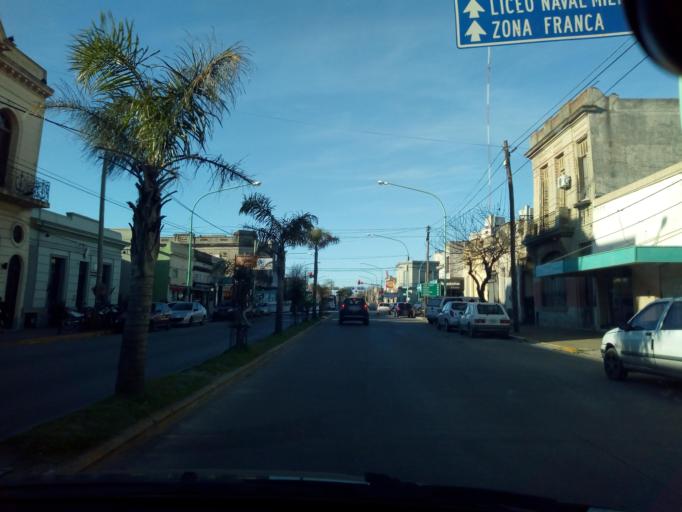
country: AR
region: Buenos Aires
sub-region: Partido de Ensenada
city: Ensenada
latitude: -34.8632
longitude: -57.9027
